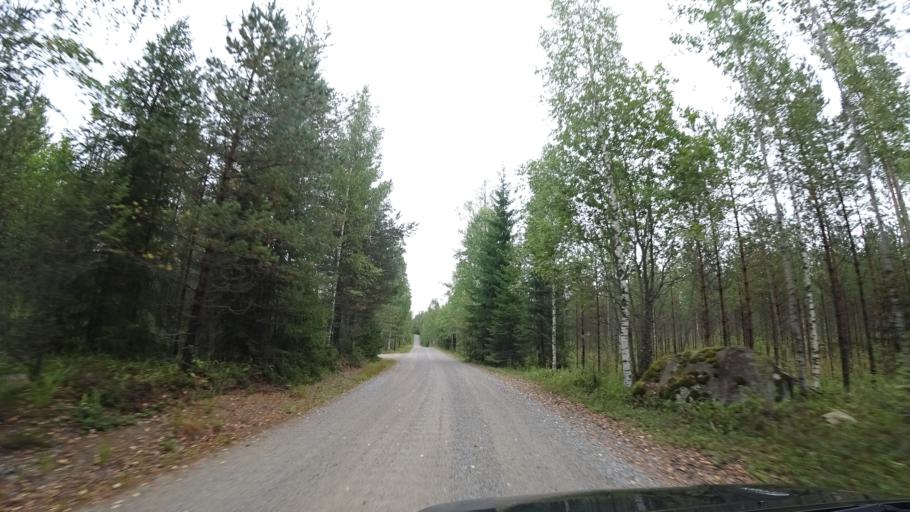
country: FI
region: Paijanne Tavastia
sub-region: Lahti
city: Auttoinen
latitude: 61.2154
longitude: 25.1251
